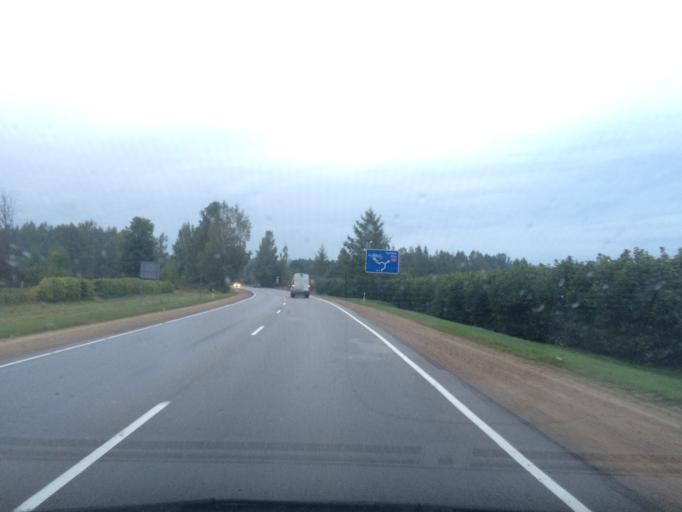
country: LV
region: Plavinu
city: Plavinas
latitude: 56.6121
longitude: 25.7846
